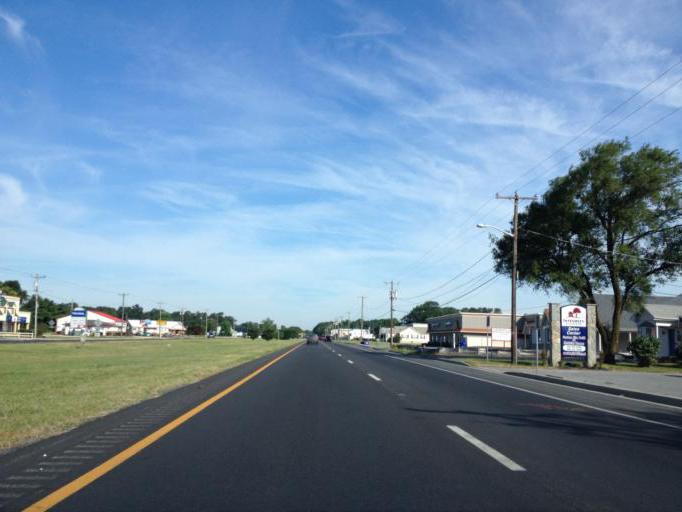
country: US
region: Delaware
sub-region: Sussex County
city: Millsboro
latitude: 38.5880
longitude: -75.2990
